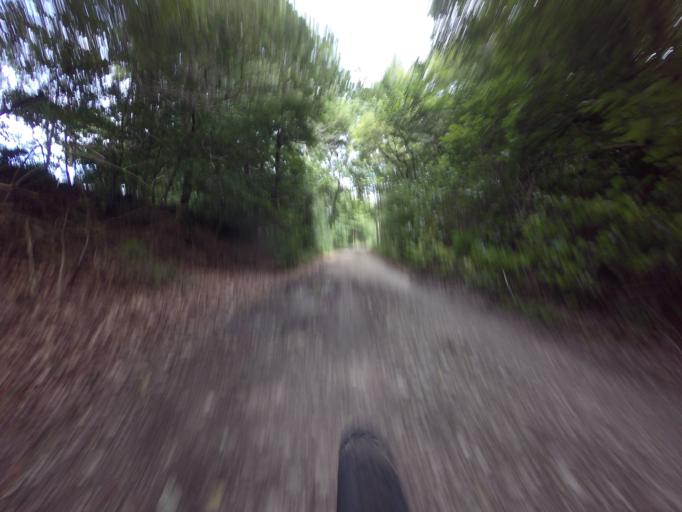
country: DK
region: Central Jutland
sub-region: Syddjurs Kommune
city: Ryomgard
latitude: 56.3999
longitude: 10.5329
